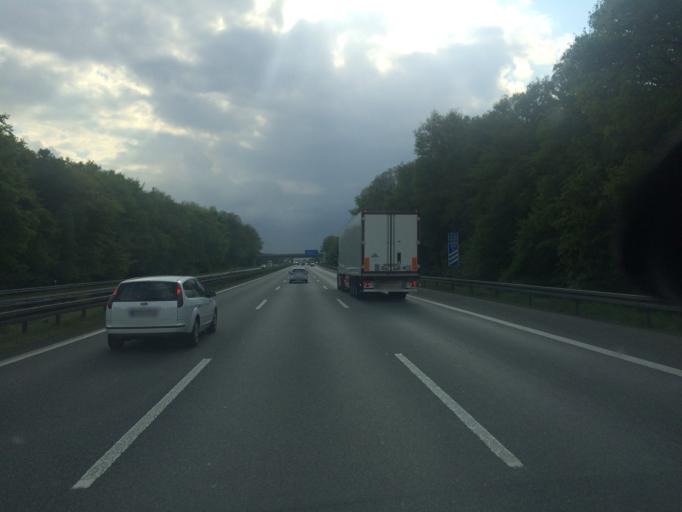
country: DE
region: North Rhine-Westphalia
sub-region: Regierungsbezirk Detmold
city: Rheda-Wiedenbruck
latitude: 51.8301
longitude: 8.2277
